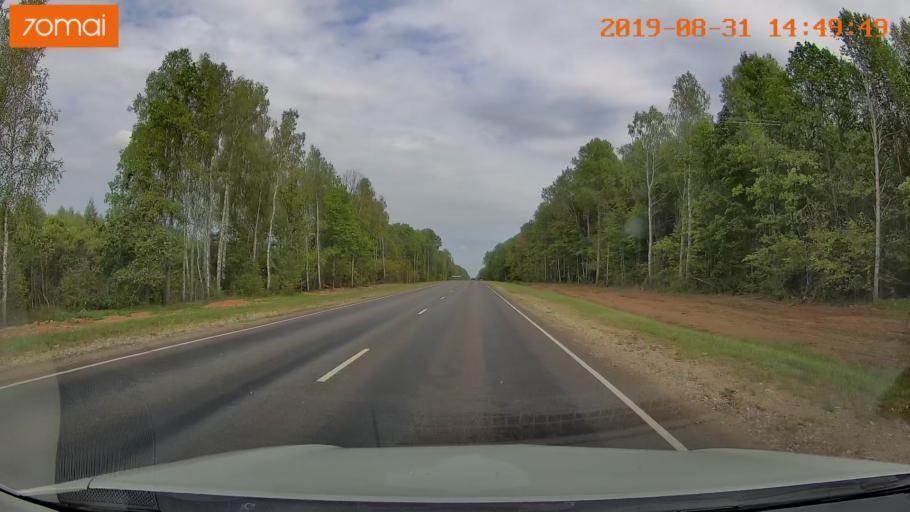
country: RU
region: Kaluga
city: Spas-Demensk
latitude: 54.2568
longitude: 33.7741
